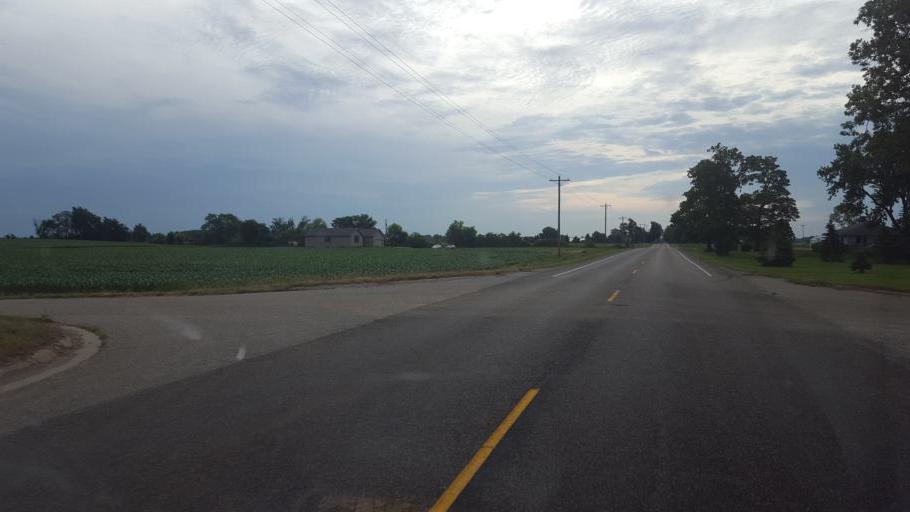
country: US
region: Michigan
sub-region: Eaton County
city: Charlotte
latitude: 42.6260
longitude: -84.8563
